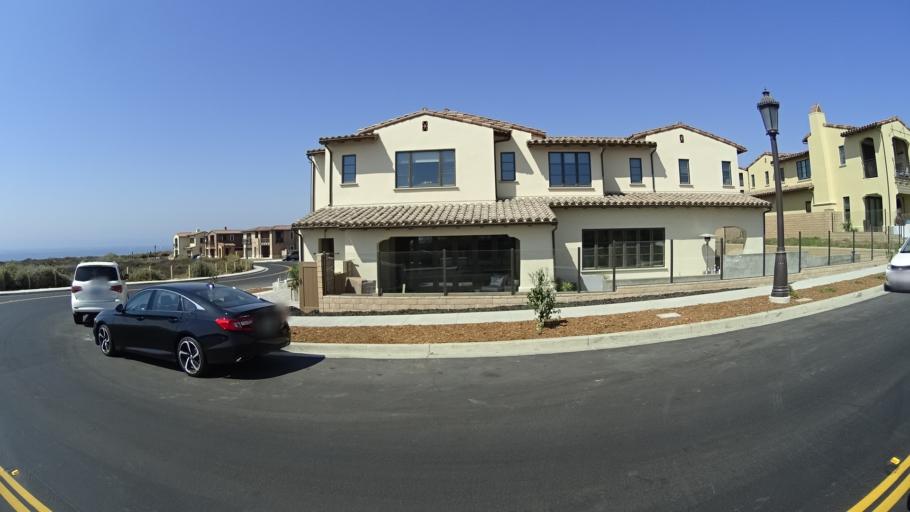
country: US
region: California
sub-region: Orange County
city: San Clemente
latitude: 33.4384
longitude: -117.6369
